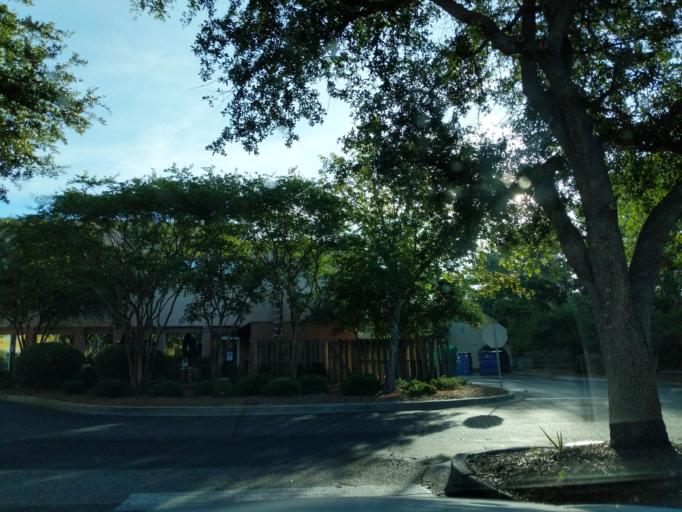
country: US
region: South Carolina
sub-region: Charleston County
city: Isle of Palms
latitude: 32.8292
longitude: -79.8240
